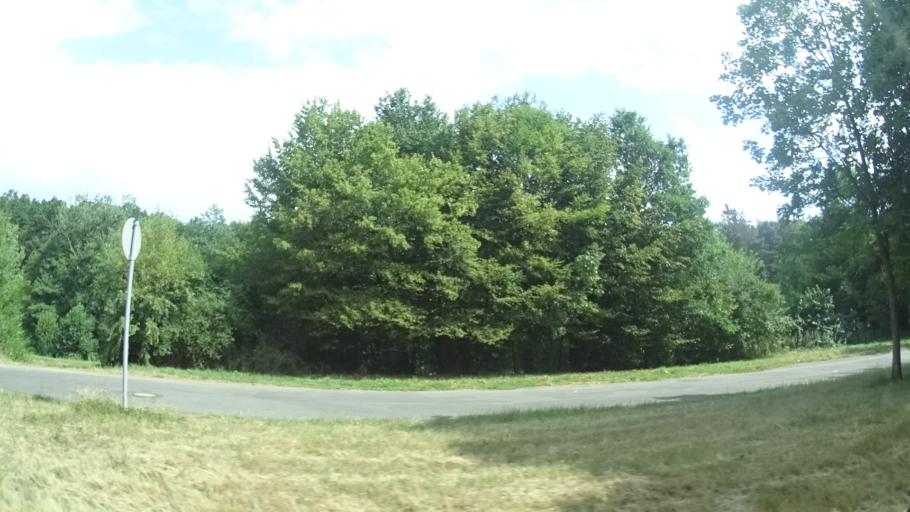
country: DE
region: Hesse
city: Grebenau
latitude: 50.7630
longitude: 9.5149
